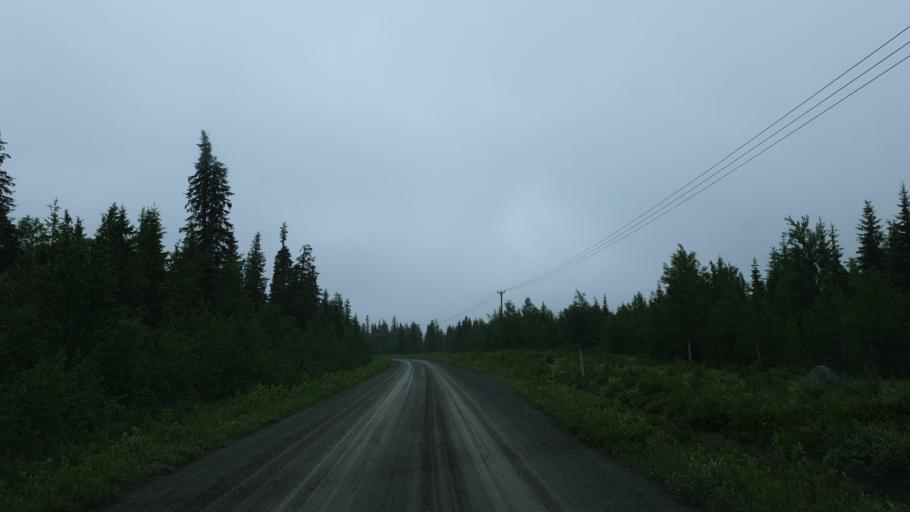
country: SE
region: Vaesterbotten
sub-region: Vilhelmina Kommun
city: Sjoberg
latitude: 65.3120
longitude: 15.9674
